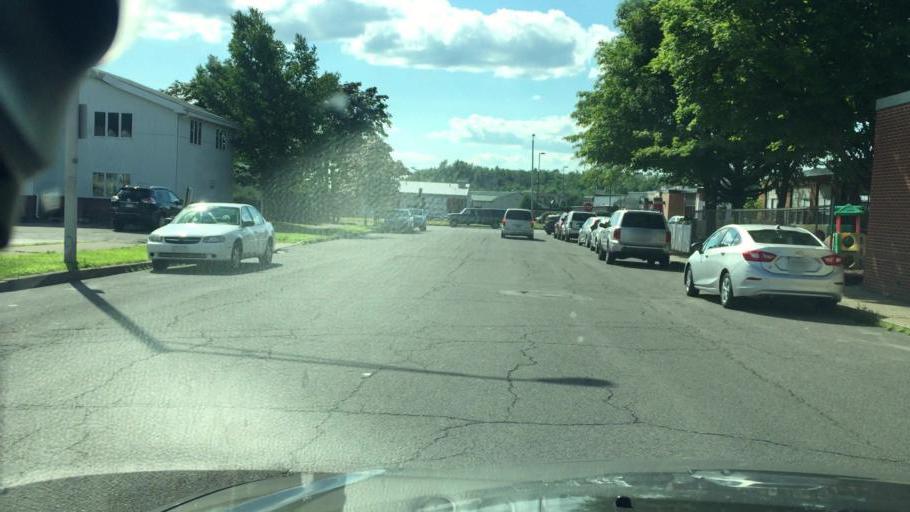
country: US
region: Pennsylvania
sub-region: Luzerne County
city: Hazleton
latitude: 40.9526
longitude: -75.9771
